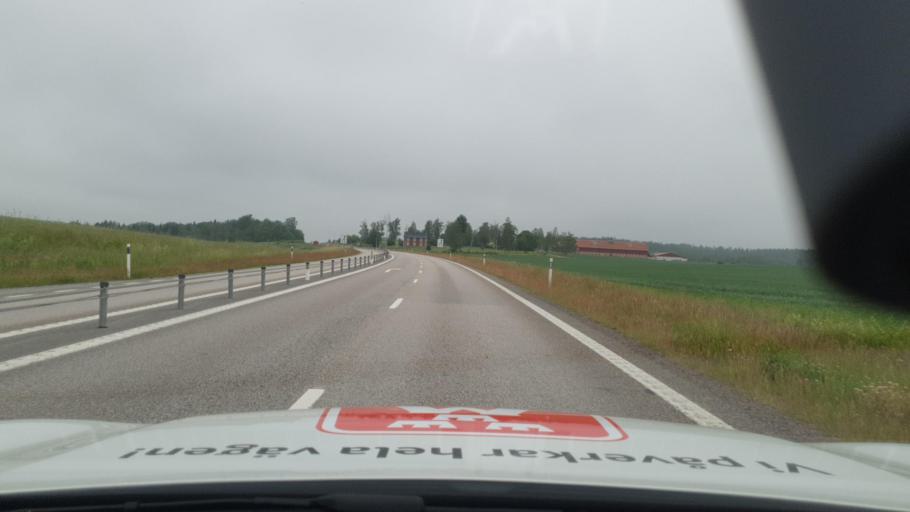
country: SE
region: Vaermland
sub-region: Karlstads Kommun
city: Edsvalla
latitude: 59.5247
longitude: 13.2150
